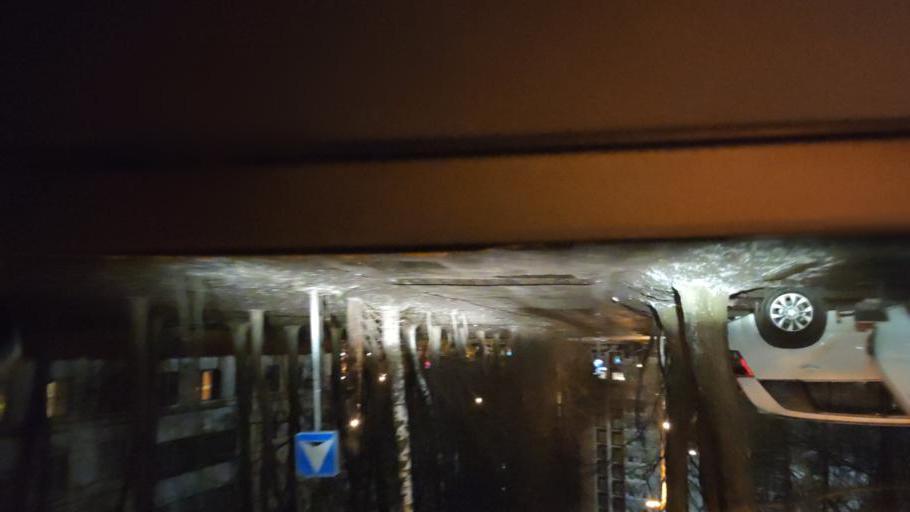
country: RU
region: Moscow
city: Strogino
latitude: 55.8506
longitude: 37.4170
